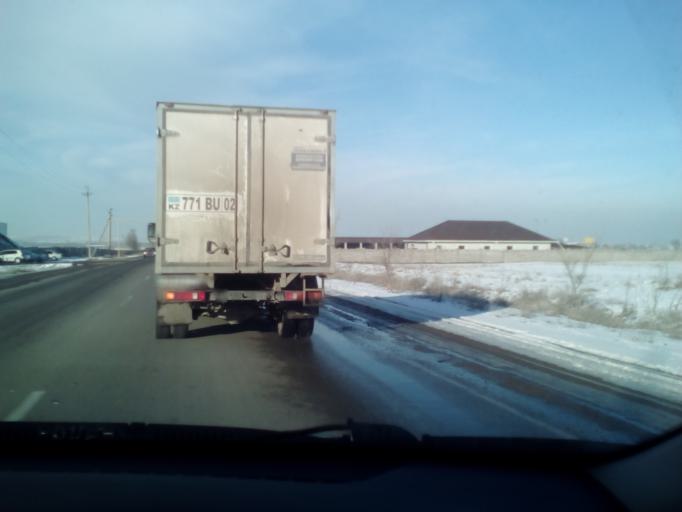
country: KZ
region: Almaty Oblysy
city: Burunday
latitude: 43.2022
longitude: 76.4149
